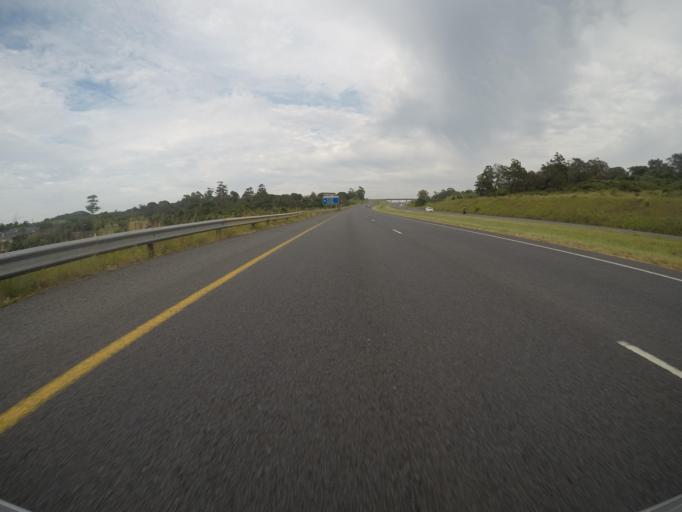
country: ZA
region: Eastern Cape
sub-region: Buffalo City Metropolitan Municipality
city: East London
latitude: -32.9713
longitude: 27.8583
